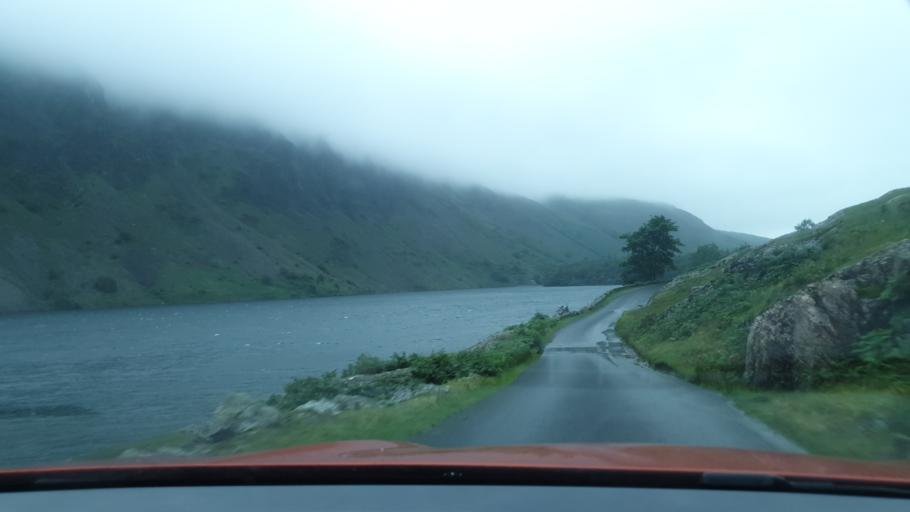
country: GB
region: England
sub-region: Cumbria
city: Seascale
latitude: 54.4337
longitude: -3.3129
